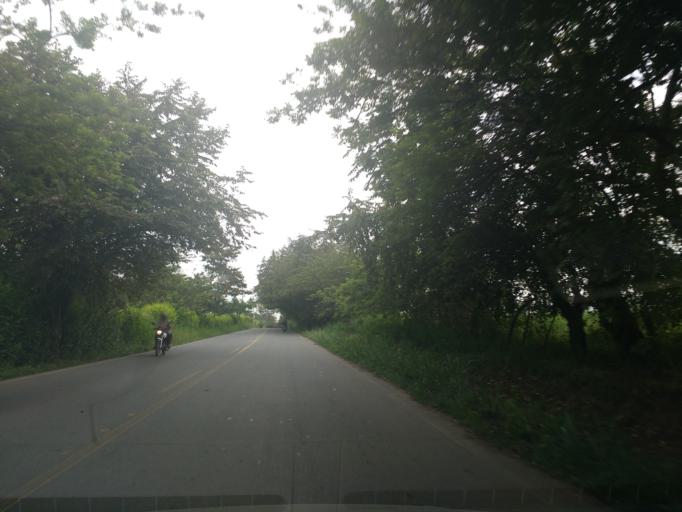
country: CO
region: Valle del Cauca
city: Florida
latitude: 3.2972
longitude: -76.2299
